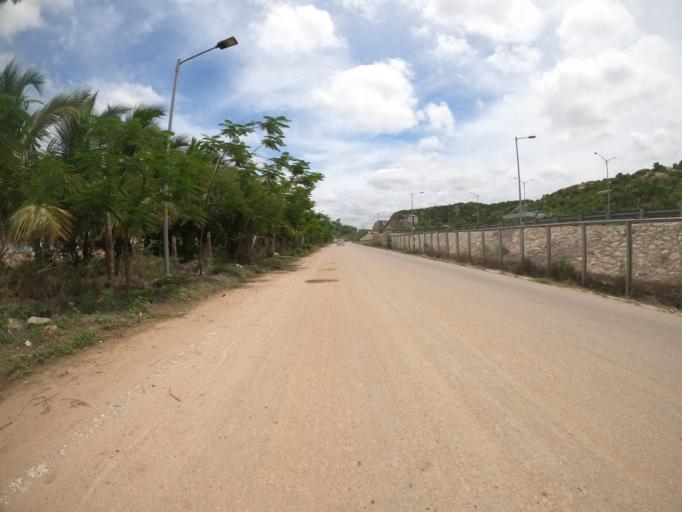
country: IN
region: Telangana
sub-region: Hyderabad
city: Hyderabad
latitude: 17.3065
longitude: 78.3774
